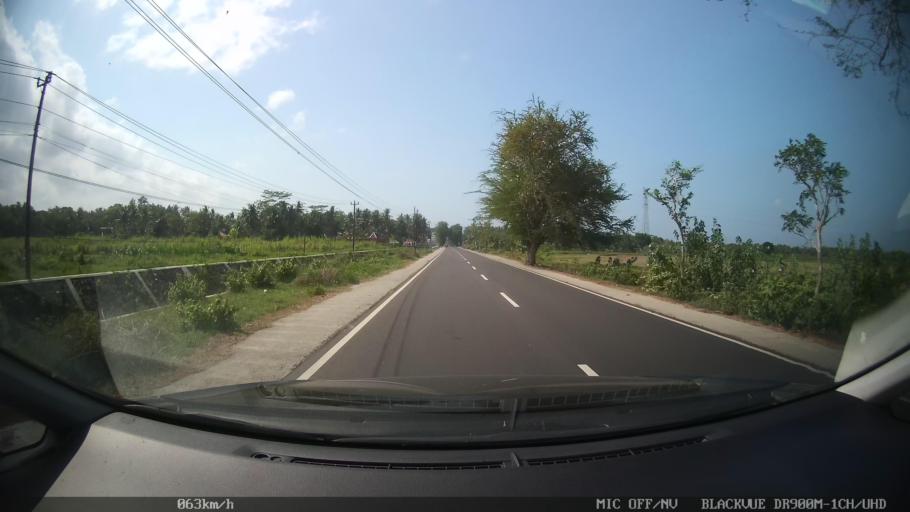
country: ID
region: Daerah Istimewa Yogyakarta
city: Srandakan
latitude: -7.8992
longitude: 110.1648
